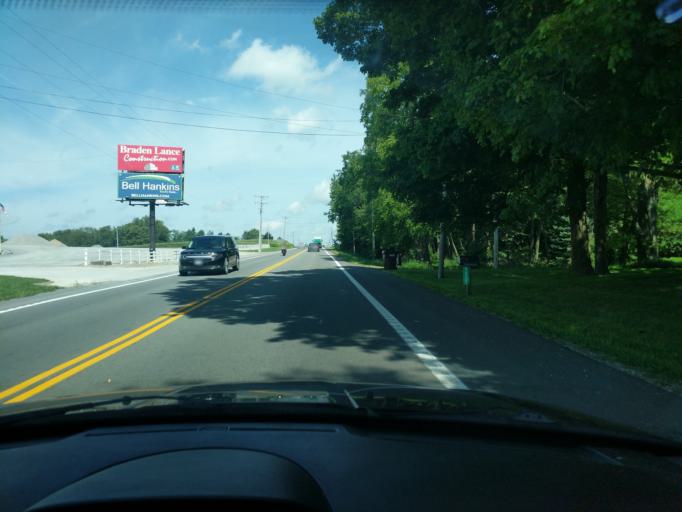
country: US
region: Ohio
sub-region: Logan County
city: West Liberty
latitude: 40.3038
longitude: -83.7594
